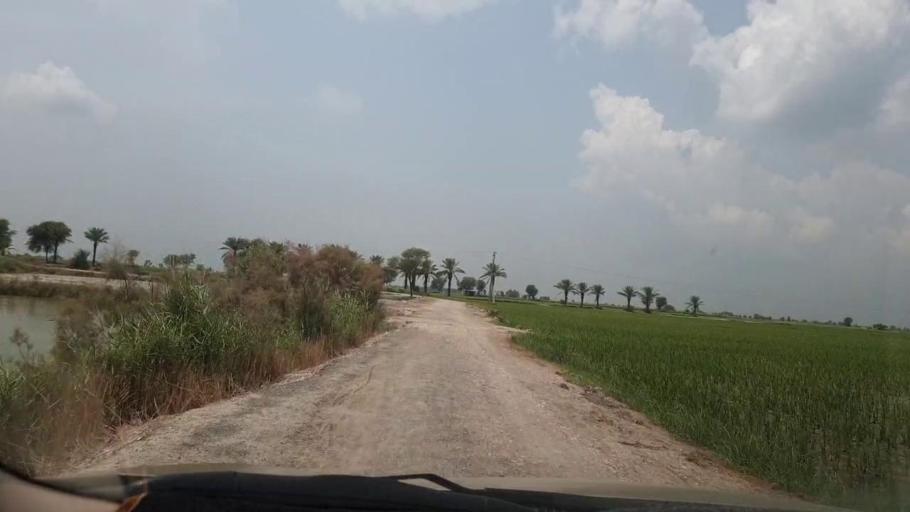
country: PK
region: Sindh
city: Larkana
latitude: 27.6150
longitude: 68.1516
